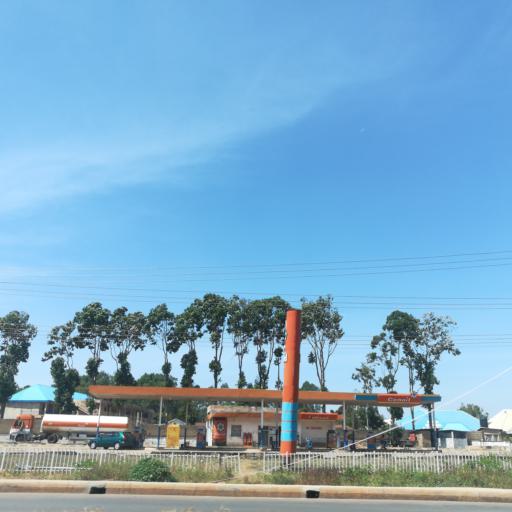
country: NG
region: Plateau
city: Bukuru
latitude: 9.7811
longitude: 8.8605
